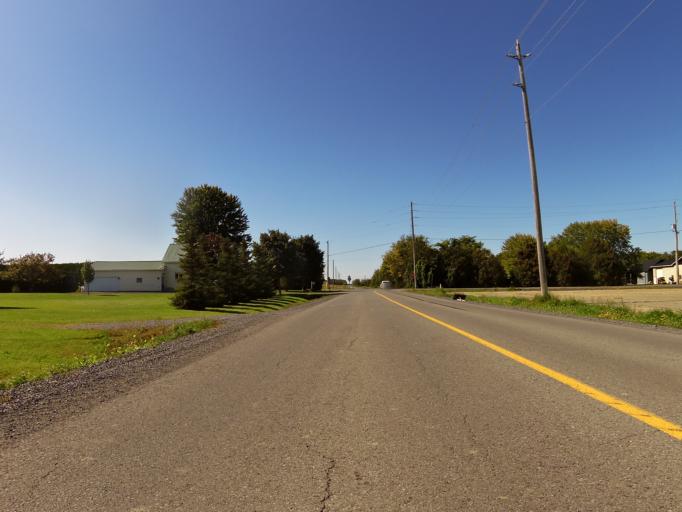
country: CA
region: Ontario
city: Casselman
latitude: 45.2618
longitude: -75.2673
